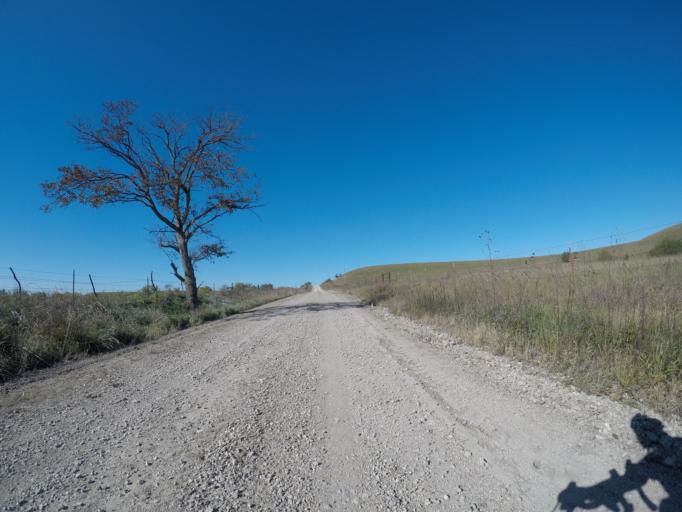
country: US
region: Kansas
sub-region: Wabaunsee County
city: Alma
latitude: 38.9132
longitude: -96.3717
